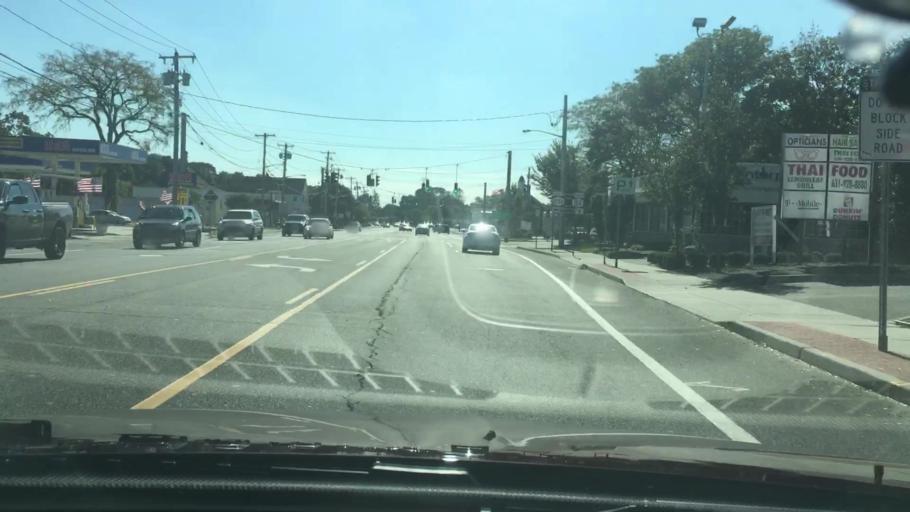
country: US
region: New York
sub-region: Suffolk County
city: Port Jefferson Station
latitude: 40.9325
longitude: -73.0533
